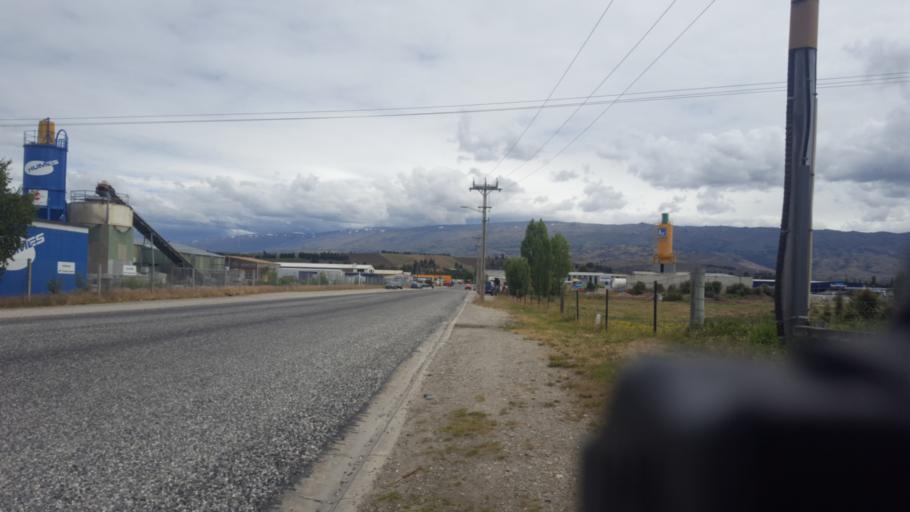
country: NZ
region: Otago
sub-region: Queenstown-Lakes District
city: Wanaka
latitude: -45.2464
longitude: 169.3755
